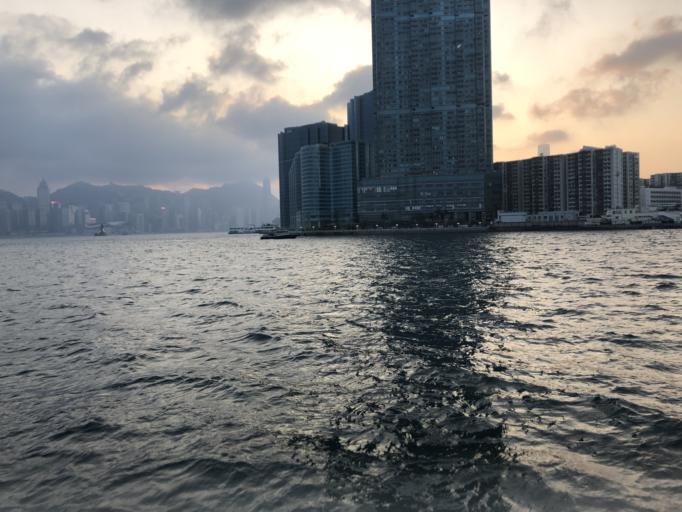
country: HK
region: Kowloon City
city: Kowloon
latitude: 22.3042
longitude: 114.1962
